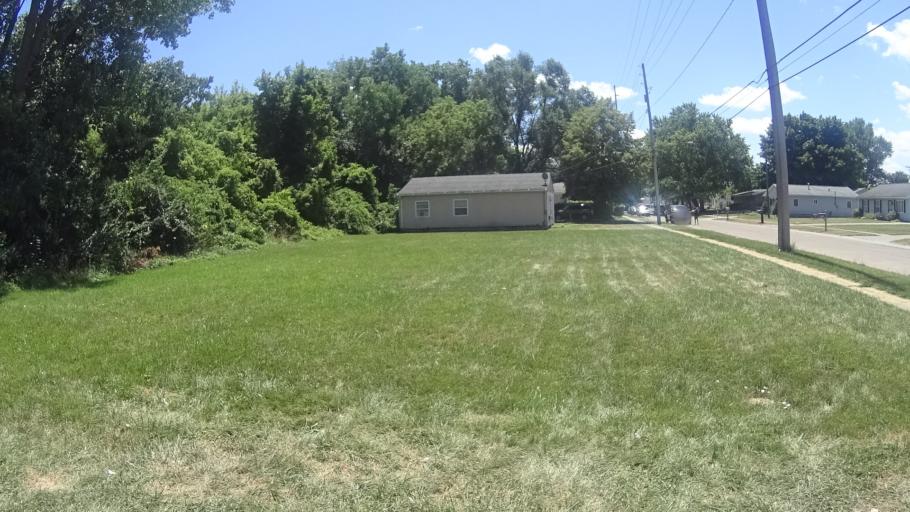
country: US
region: Ohio
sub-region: Erie County
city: Sandusky
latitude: 41.4462
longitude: -82.6831
